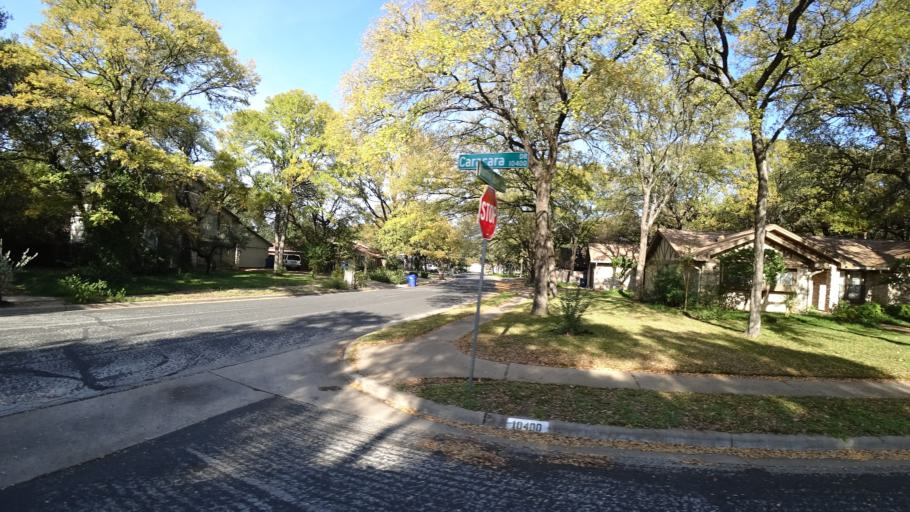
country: US
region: Texas
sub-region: Williamson County
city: Anderson Mill
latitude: 30.4491
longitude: -97.8052
